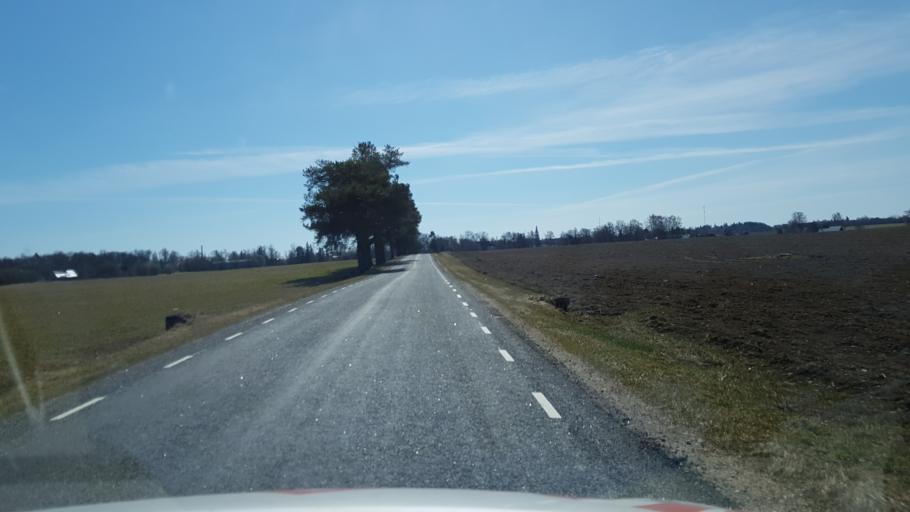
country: EE
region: Laeaene-Virumaa
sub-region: Vinni vald
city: Vinni
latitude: 59.1055
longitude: 26.5255
